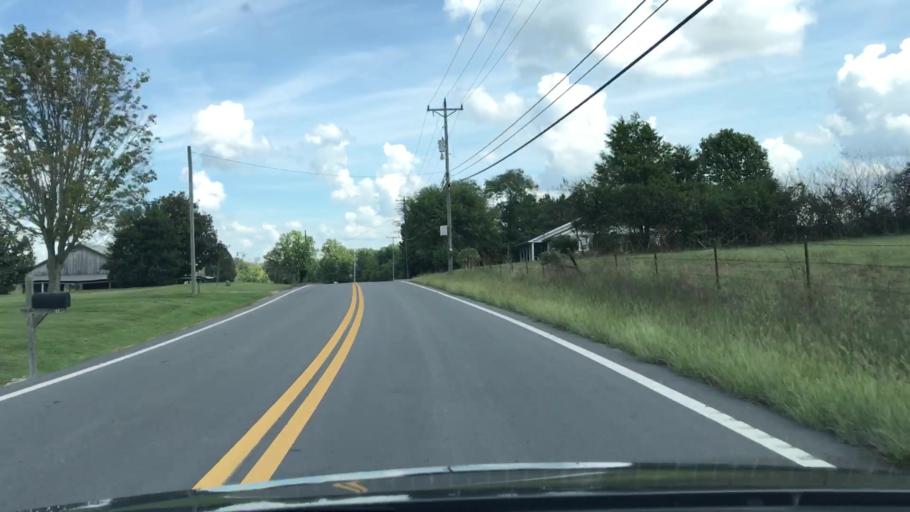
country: US
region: Tennessee
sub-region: Sumner County
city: Portland
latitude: 36.5369
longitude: -86.5269
